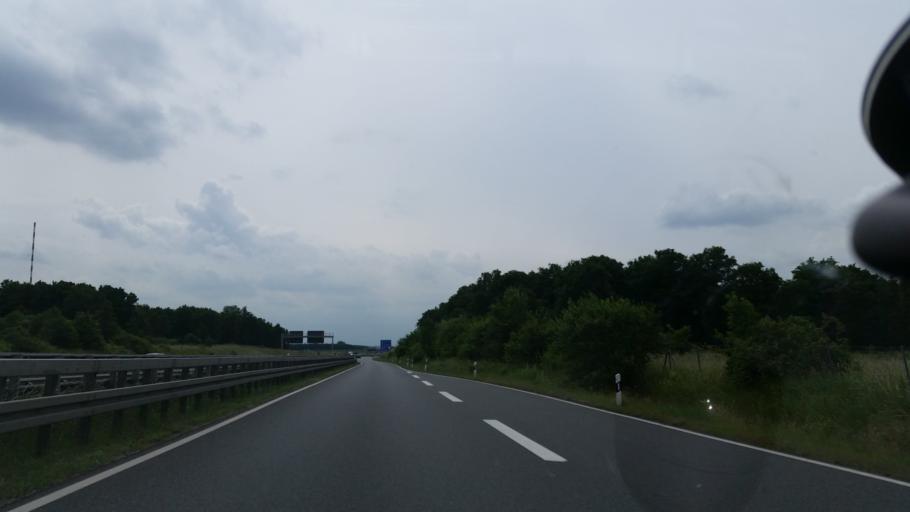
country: DE
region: Lower Saxony
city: Lehre
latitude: 52.3051
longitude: 10.7253
